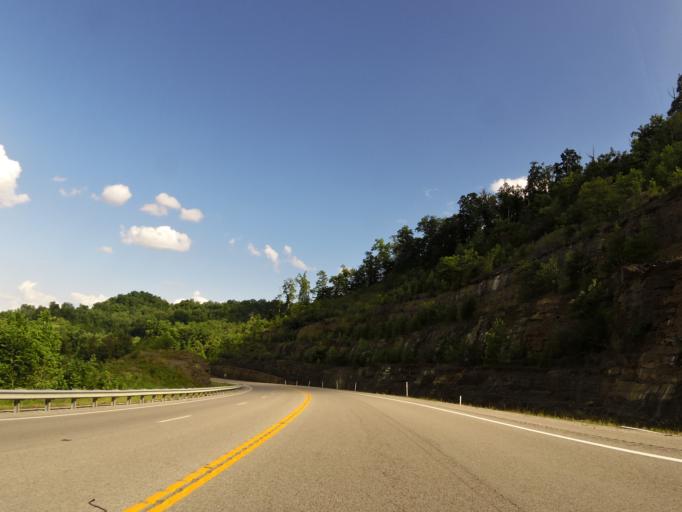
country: US
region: Kentucky
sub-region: Harlan County
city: Harlan
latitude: 36.7938
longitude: -83.2674
